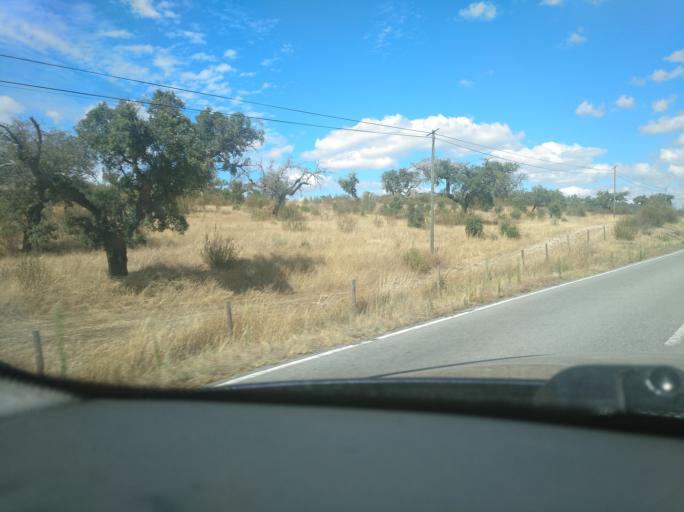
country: ES
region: Extremadura
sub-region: Provincia de Badajoz
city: La Codosera
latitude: 39.1484
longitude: -7.2150
